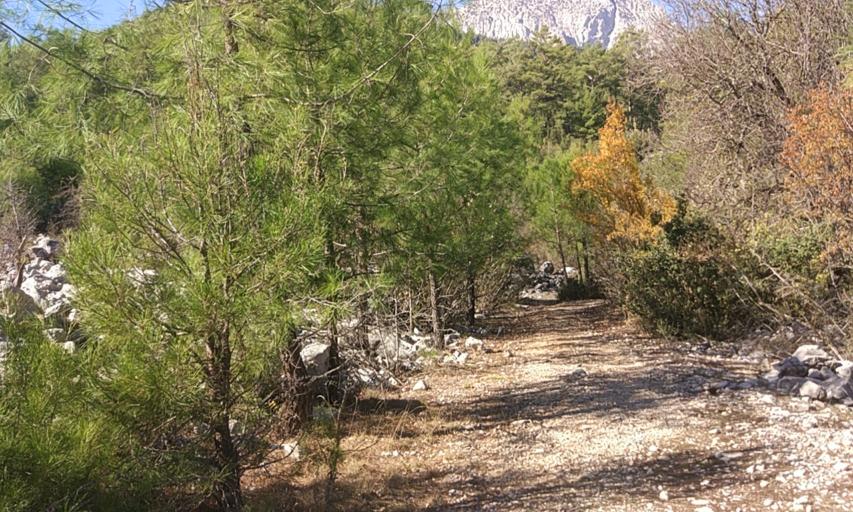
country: TR
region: Antalya
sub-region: Kemer
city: Goeynuek
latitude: 36.6354
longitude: 30.4478
